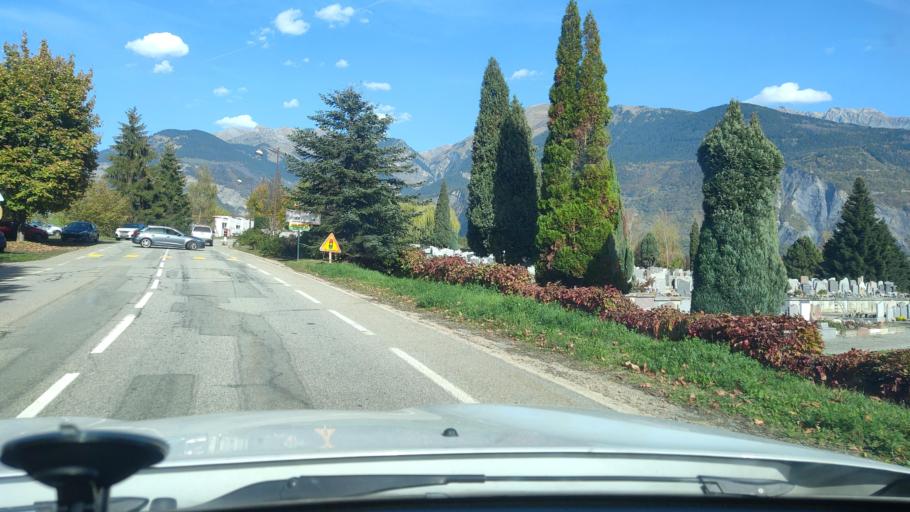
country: FR
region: Rhone-Alpes
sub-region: Departement de la Savoie
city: Saint-Jean-de-Maurienne
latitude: 45.2681
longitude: 6.3398
